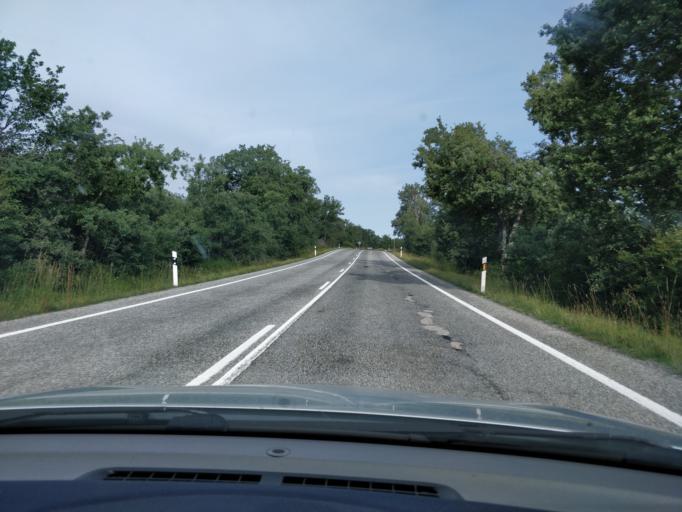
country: ES
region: Cantabria
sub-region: Provincia de Cantabria
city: San Martin de Elines
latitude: 42.9590
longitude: -3.7722
